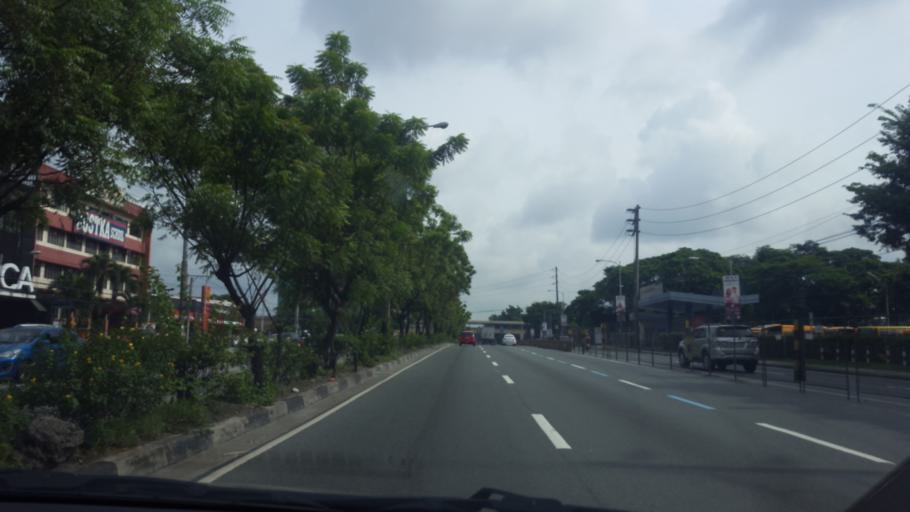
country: PH
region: Metro Manila
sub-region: Marikina
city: Calumpang
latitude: 14.6350
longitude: 121.0743
